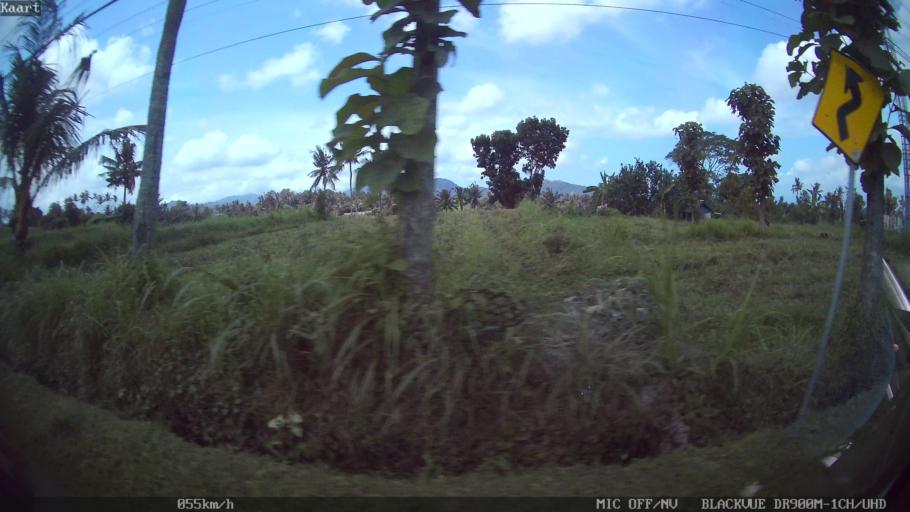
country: ID
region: Bali
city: Banjar Kelodan
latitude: -8.5132
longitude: 115.3805
